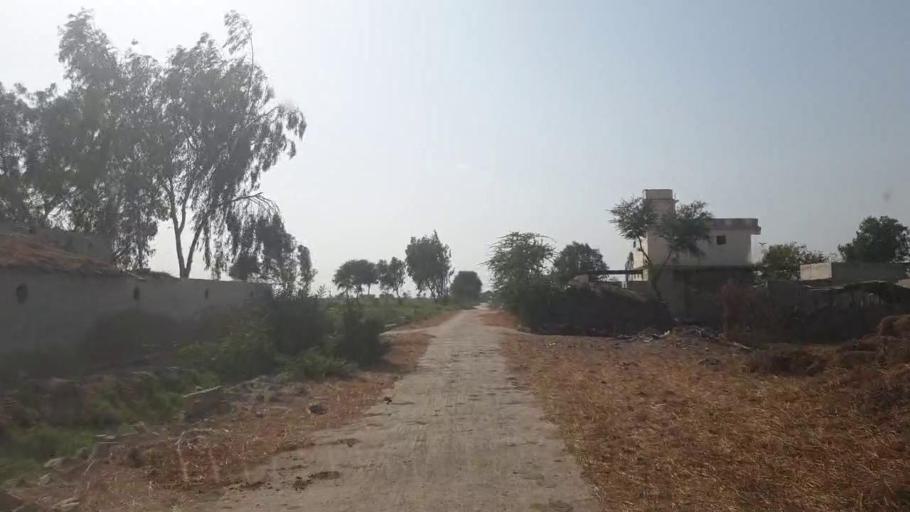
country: PK
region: Sindh
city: Kario
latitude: 24.5532
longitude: 68.5067
